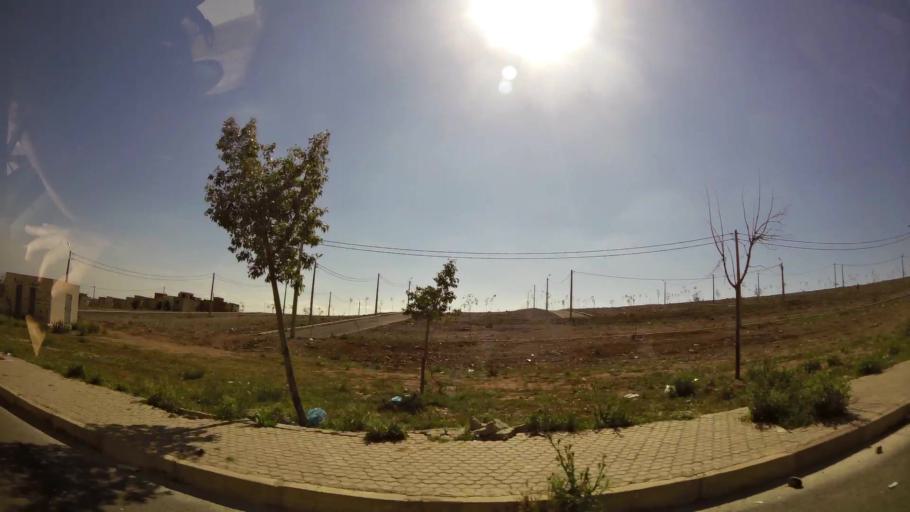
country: MA
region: Oriental
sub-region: Oujda-Angad
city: Oujda
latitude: 34.6547
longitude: -1.9417
